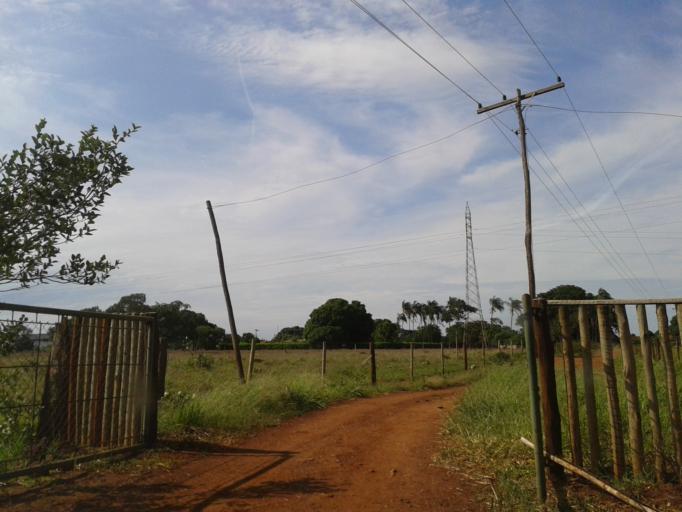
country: BR
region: Minas Gerais
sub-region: Centralina
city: Centralina
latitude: -18.7142
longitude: -49.2008
